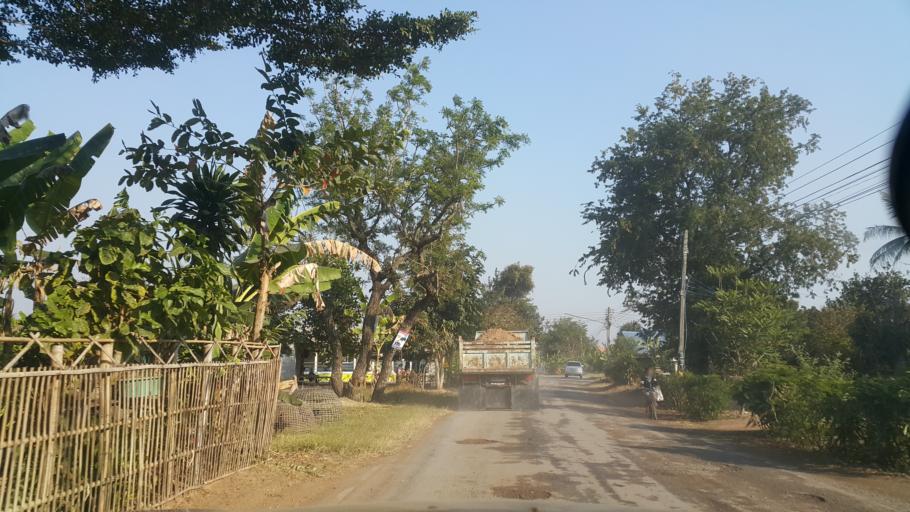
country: TH
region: Nakhon Ratchasima
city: Chakkarat
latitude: 15.0688
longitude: 102.3964
